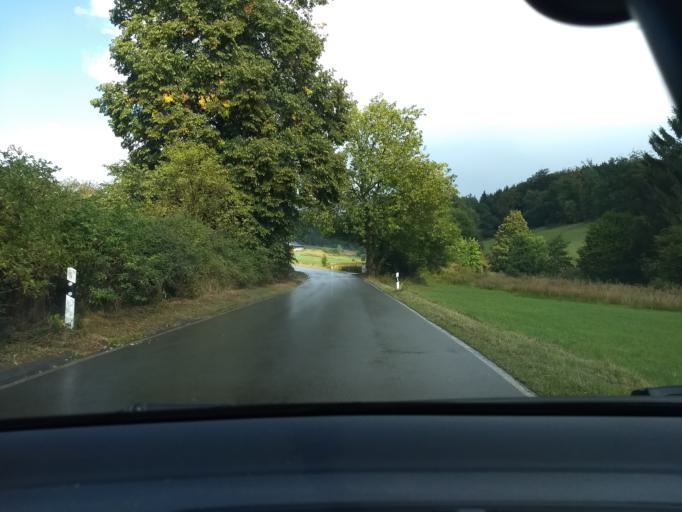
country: DE
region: North Rhine-Westphalia
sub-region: Regierungsbezirk Arnsberg
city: Finnentrop
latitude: 51.2222
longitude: 8.0383
